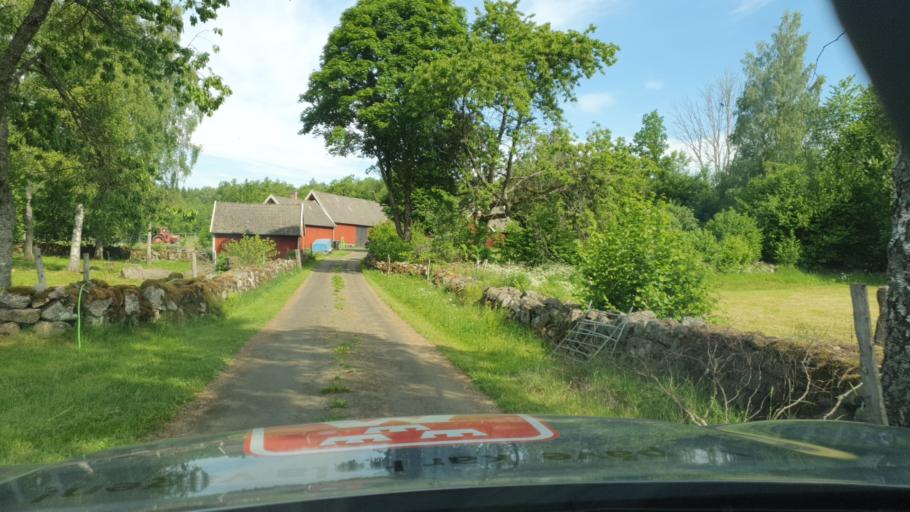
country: SE
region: Skane
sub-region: Hassleholms Kommun
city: Vinslov
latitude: 56.0428
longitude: 13.8681
